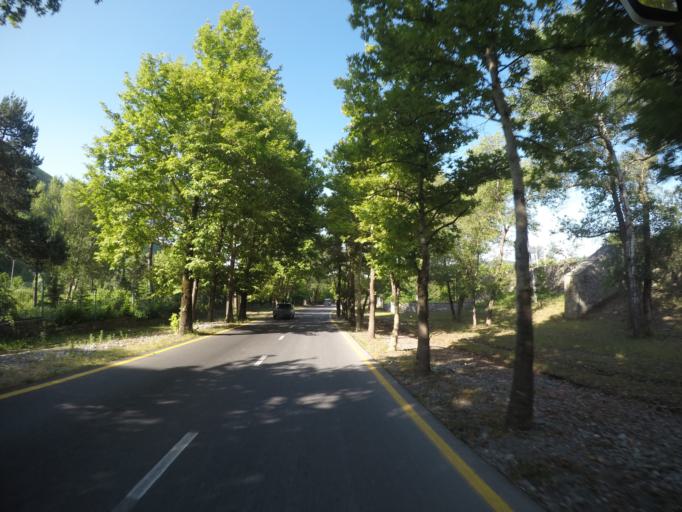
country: AZ
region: Shaki City
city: Sheki
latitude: 41.2400
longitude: 47.1851
